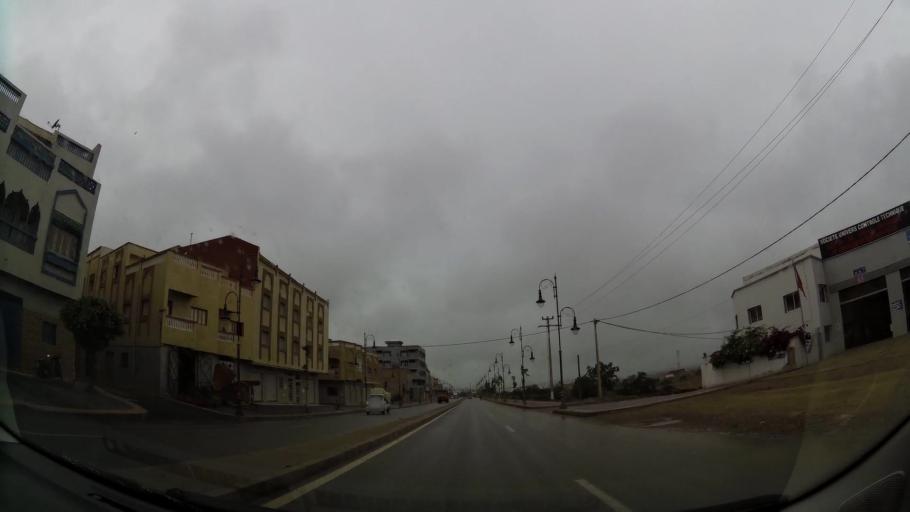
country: MA
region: Taza-Al Hoceima-Taounate
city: Imzourene
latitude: 35.1660
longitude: -3.8571
